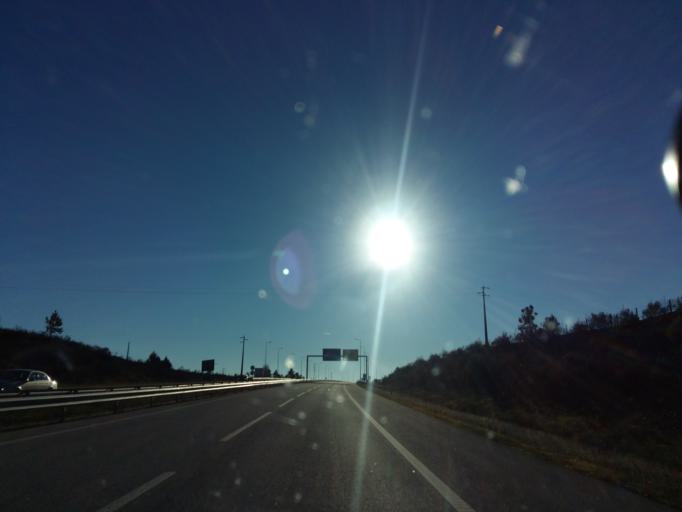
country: PT
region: Castelo Branco
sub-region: Castelo Branco
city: Castelo Branco
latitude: 39.7905
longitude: -7.5655
